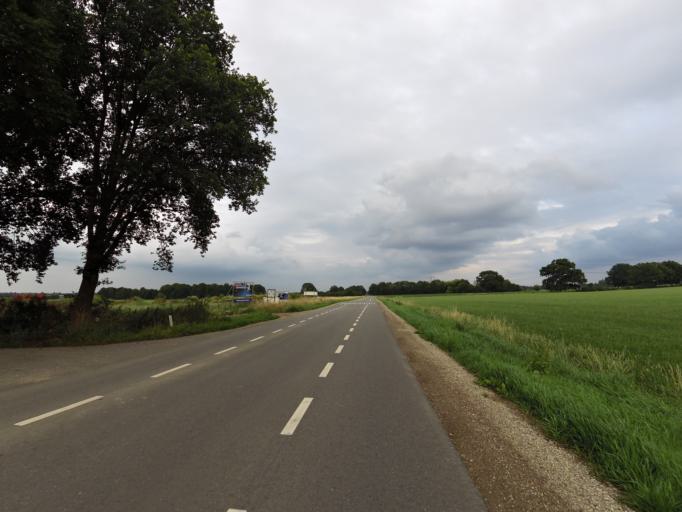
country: NL
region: Gelderland
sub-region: Gemeente Doesburg
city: Doesburg
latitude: 51.9854
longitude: 6.1998
